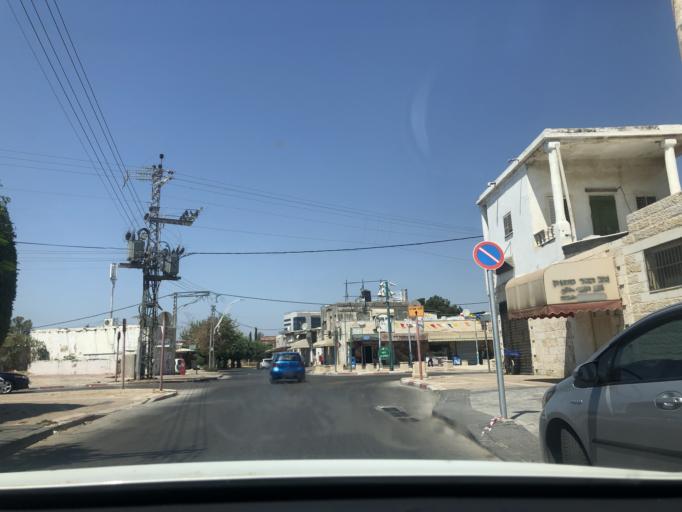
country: IL
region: Central District
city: Lod
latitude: 31.9563
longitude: 34.8967
